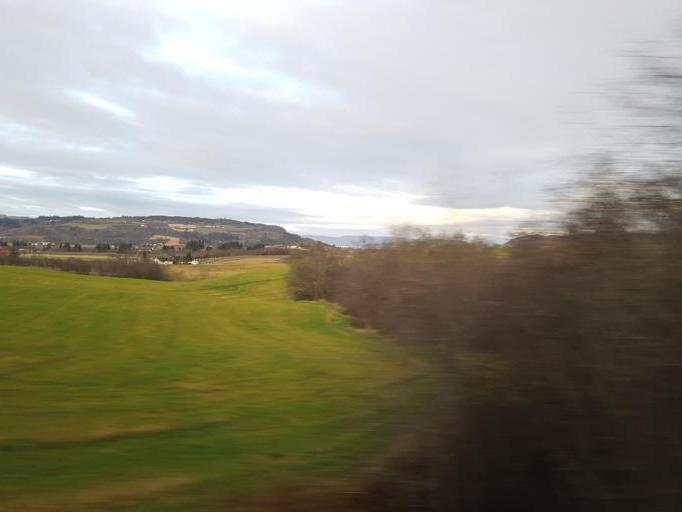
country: NO
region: Sor-Trondelag
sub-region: Melhus
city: Melhus
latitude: 63.3156
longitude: 10.3038
